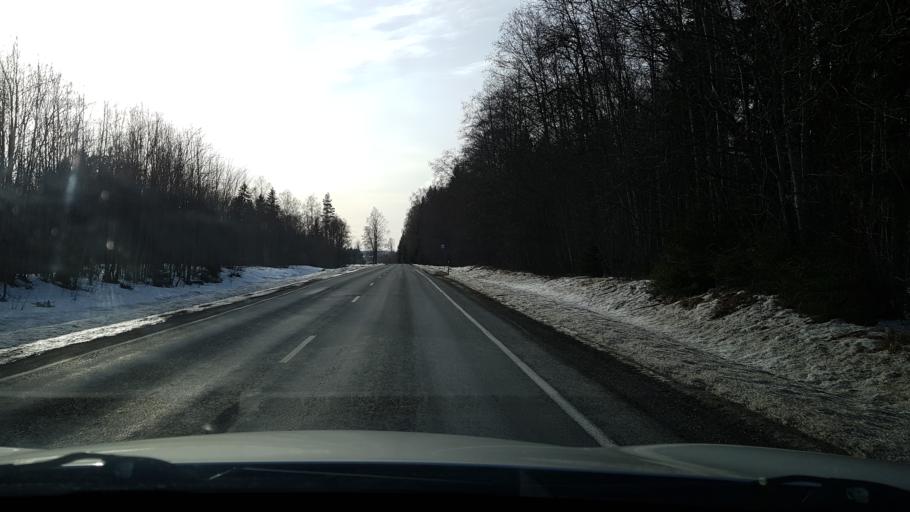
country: EE
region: Viljandimaa
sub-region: Suure-Jaani vald
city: Suure-Jaani
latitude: 58.3462
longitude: 25.3607
